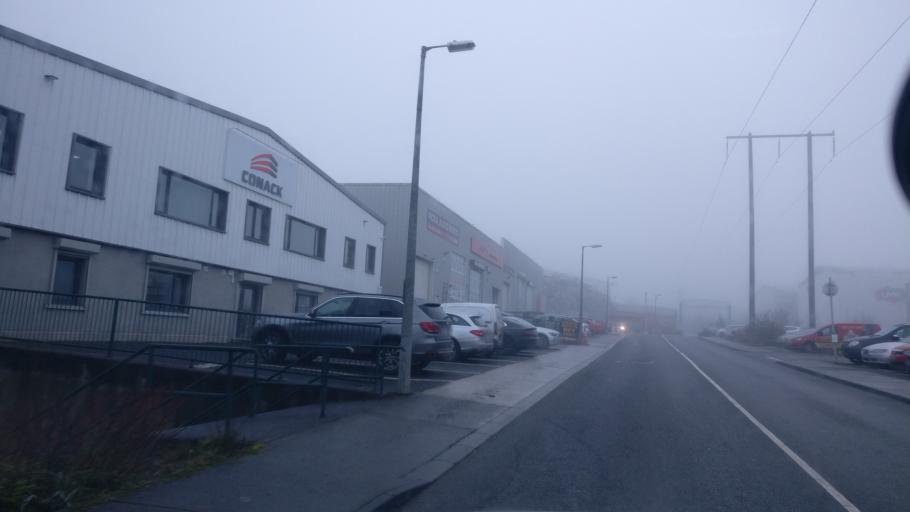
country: IE
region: Munster
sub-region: County Limerick
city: Luimneach
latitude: 52.6487
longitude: -8.5857
